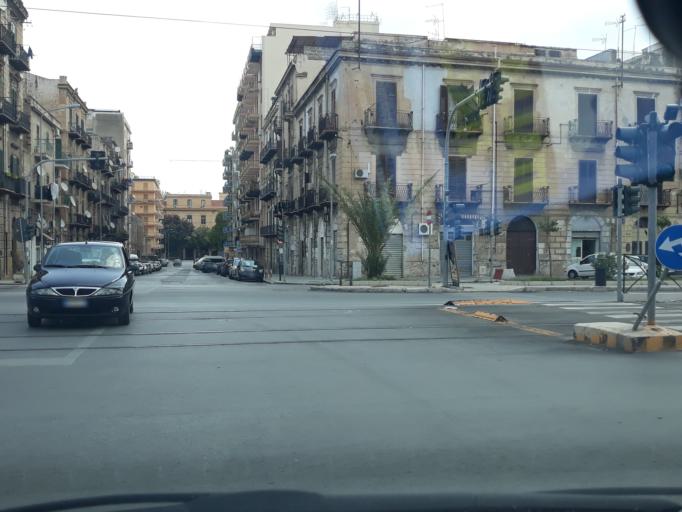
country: IT
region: Sicily
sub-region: Palermo
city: Palermo
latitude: 38.1087
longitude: 13.3705
